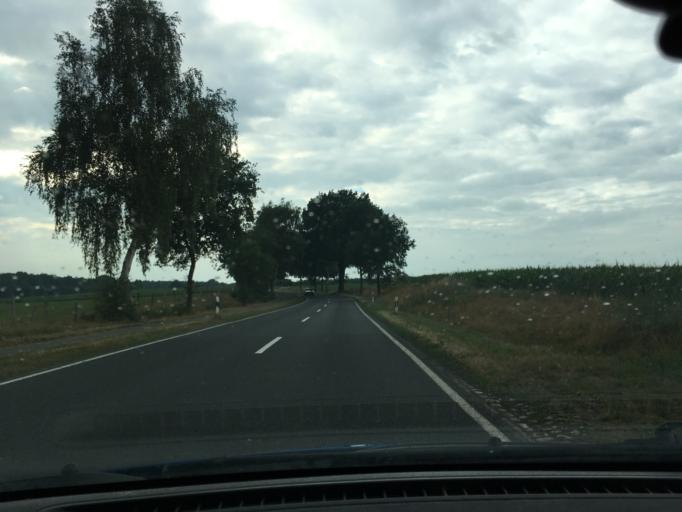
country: DE
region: Lower Saxony
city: Wenzendorf
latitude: 53.3504
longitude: 9.7478
